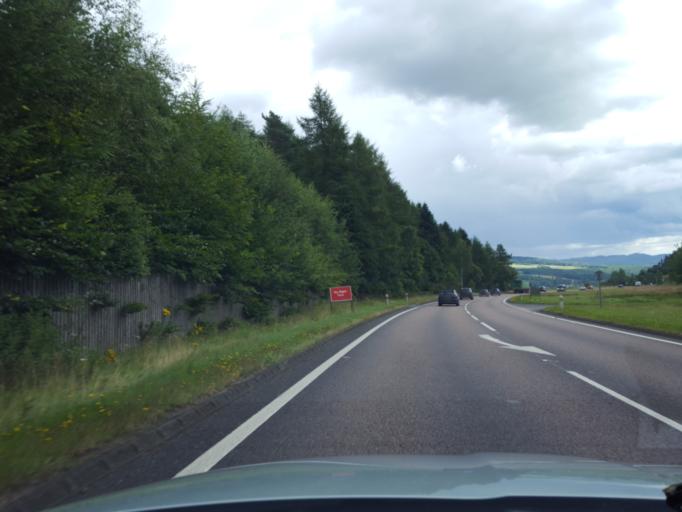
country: GB
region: Scotland
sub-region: Perth and Kinross
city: Pitlochry
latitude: 56.6967
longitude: -3.7347
